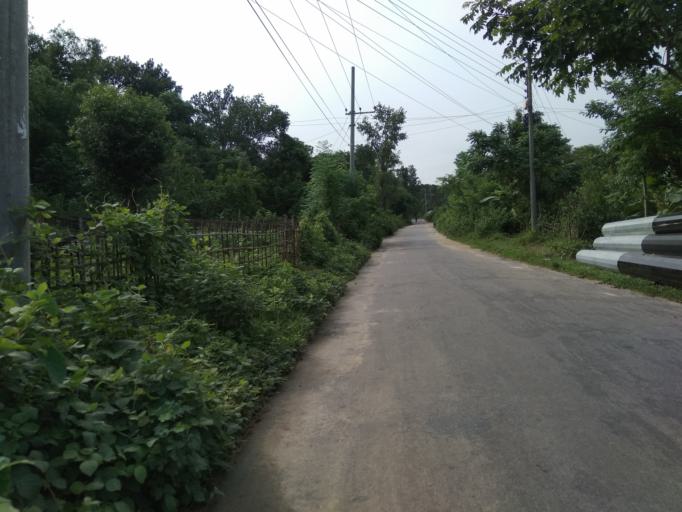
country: BD
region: Chittagong
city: Khagrachhari
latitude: 23.0373
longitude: 92.0046
